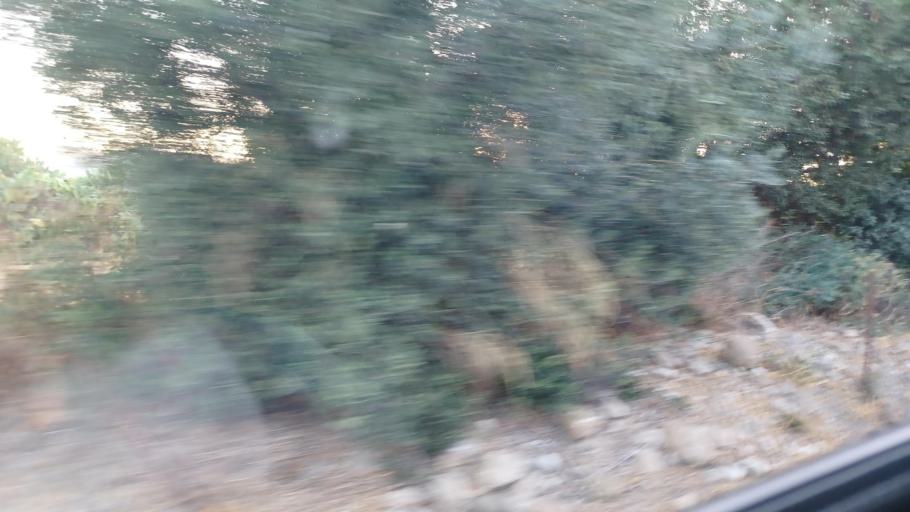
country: CY
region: Pafos
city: Mesogi
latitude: 34.8262
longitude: 32.5791
